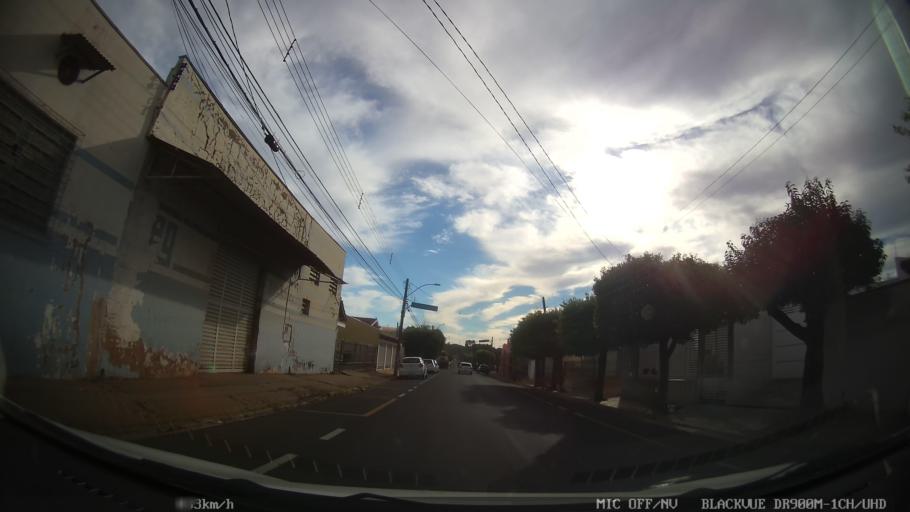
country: BR
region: Sao Paulo
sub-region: Catanduva
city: Catanduva
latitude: -21.1211
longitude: -48.9667
